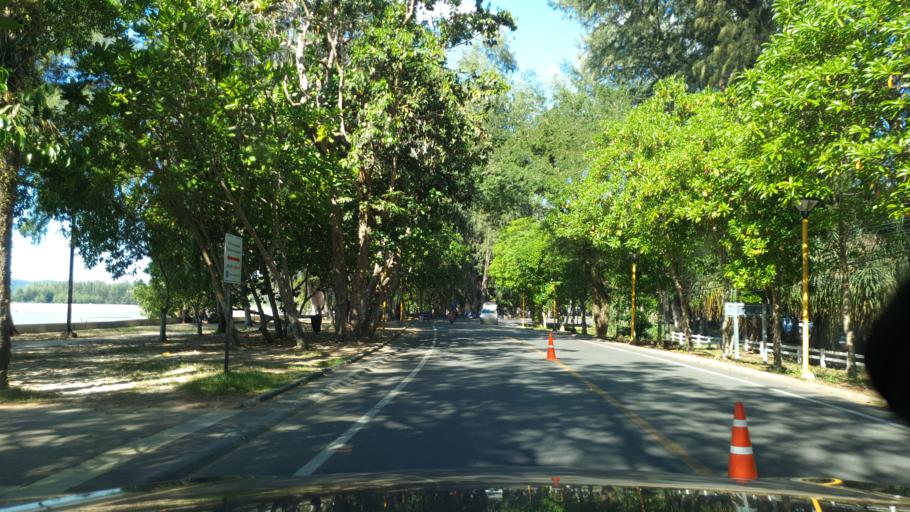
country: TH
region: Phangnga
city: Ban Ao Nang
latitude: 8.0459
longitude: 98.8032
